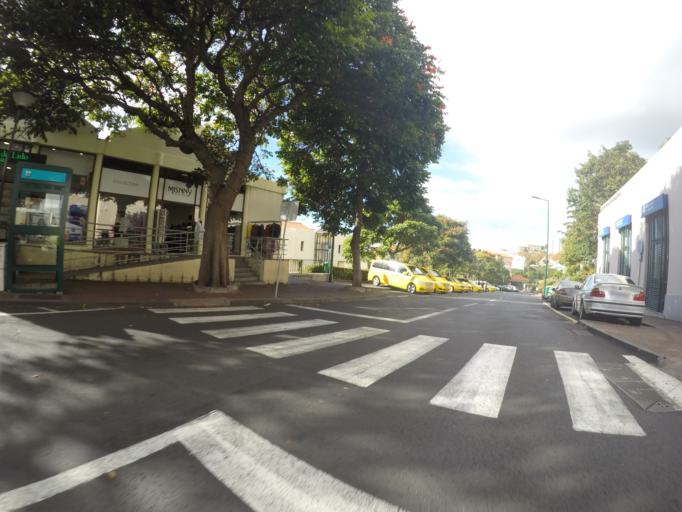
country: PT
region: Madeira
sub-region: Funchal
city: Funchal
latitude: 32.6380
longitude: -16.9316
